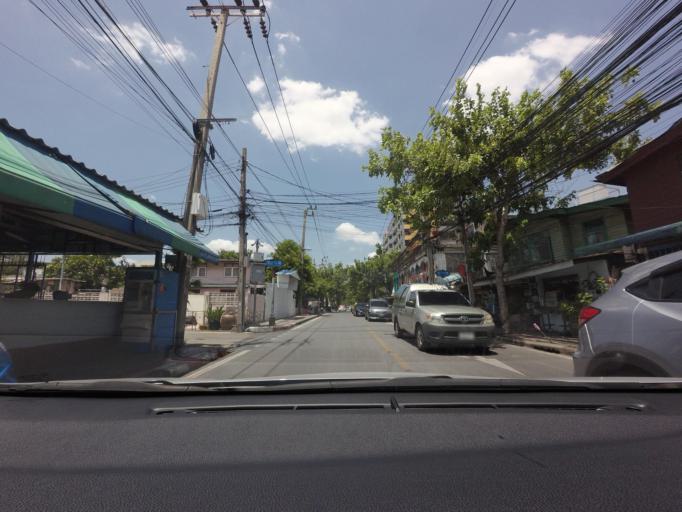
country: TH
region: Bangkok
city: Bang Na
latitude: 13.6888
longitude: 100.6352
